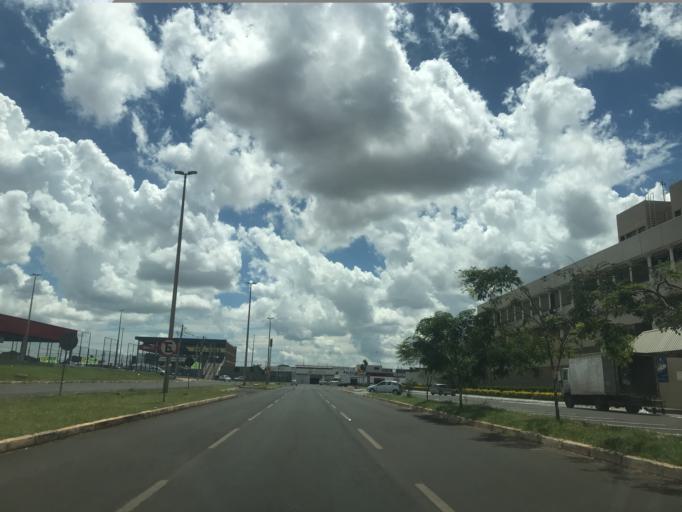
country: BR
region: Federal District
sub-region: Brasilia
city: Brasilia
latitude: -15.8474
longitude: -48.0399
